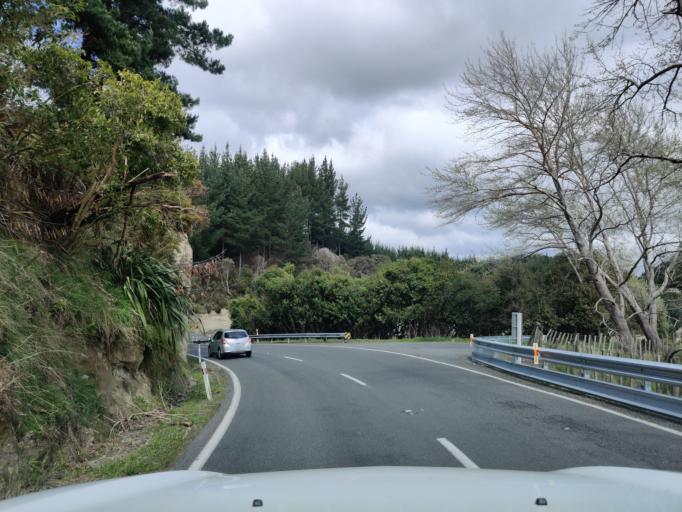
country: NZ
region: Manawatu-Wanganui
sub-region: Wanganui District
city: Wanganui
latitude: -39.7968
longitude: 175.1988
